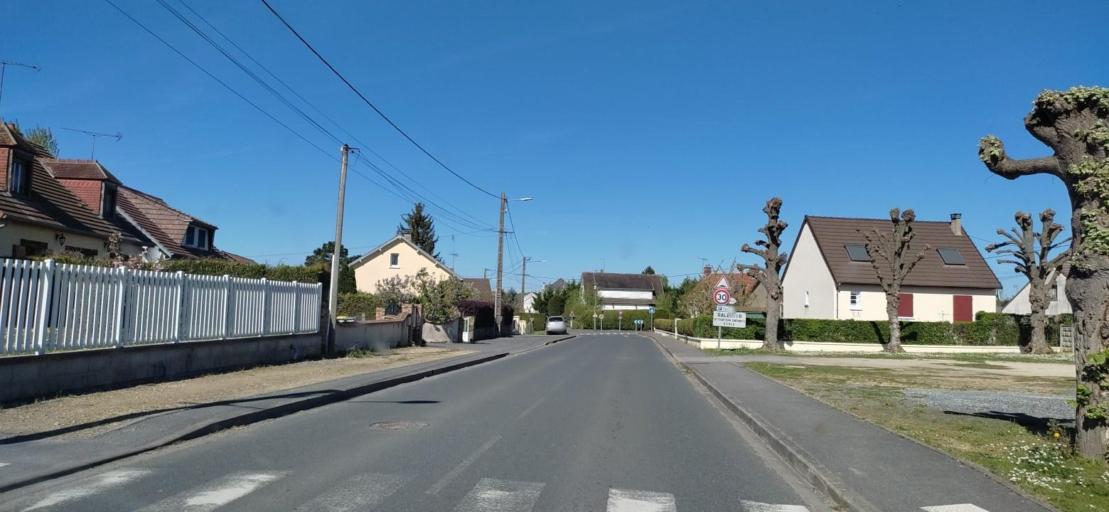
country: FR
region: Picardie
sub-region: Departement de l'Oise
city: Tracy-le-Mont
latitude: 49.4963
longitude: 2.9703
